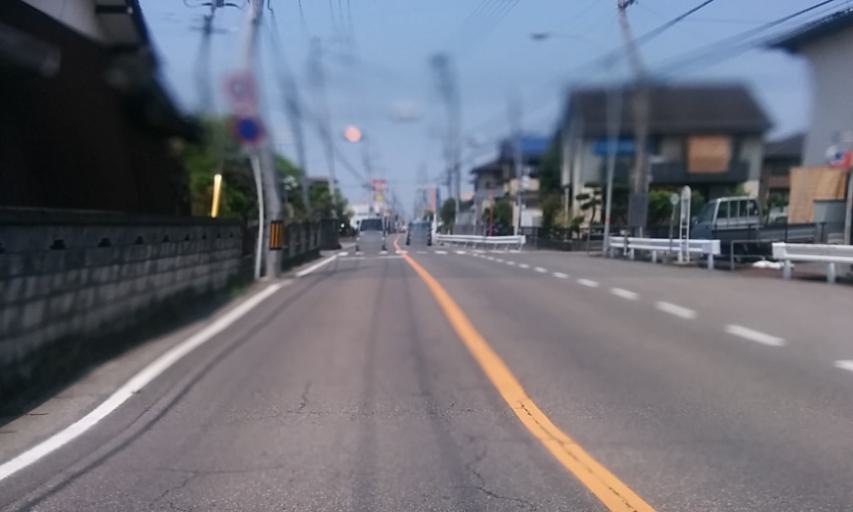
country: JP
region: Ehime
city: Niihama
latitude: 33.9274
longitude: 133.3004
